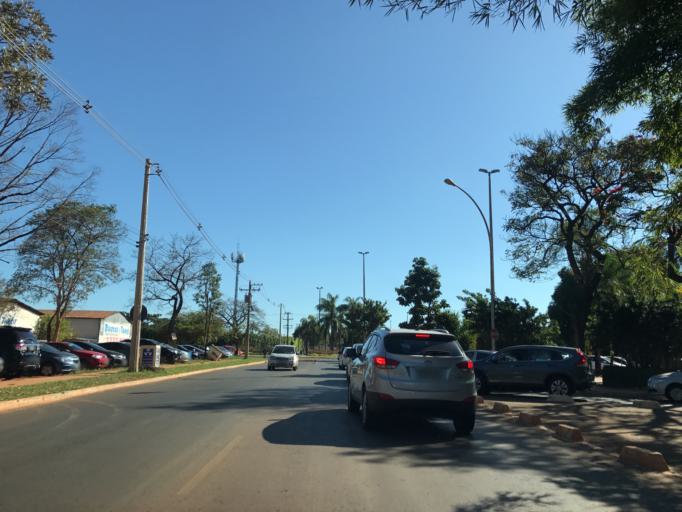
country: BR
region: Federal District
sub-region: Brasilia
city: Brasilia
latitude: -15.8259
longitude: -47.9310
